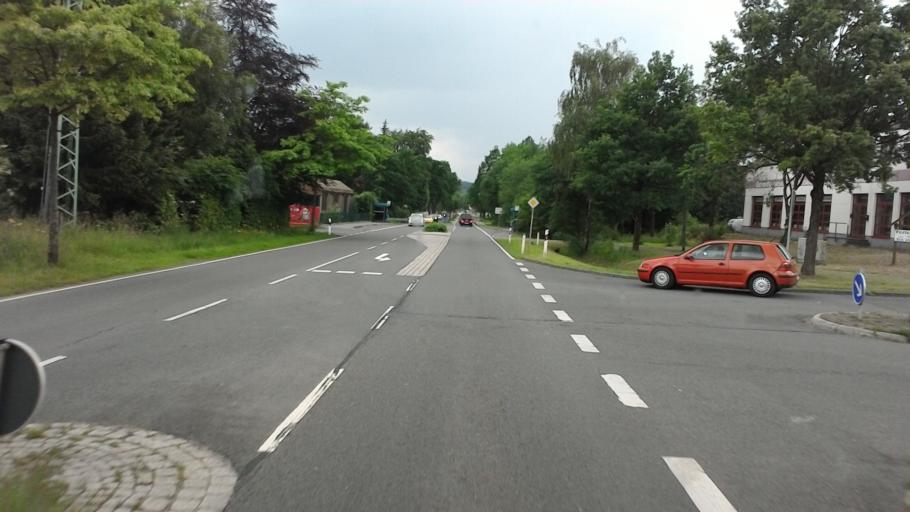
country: DE
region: North Rhine-Westphalia
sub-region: Regierungsbezirk Koln
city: Roetgen
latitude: 50.6527
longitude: 6.1860
